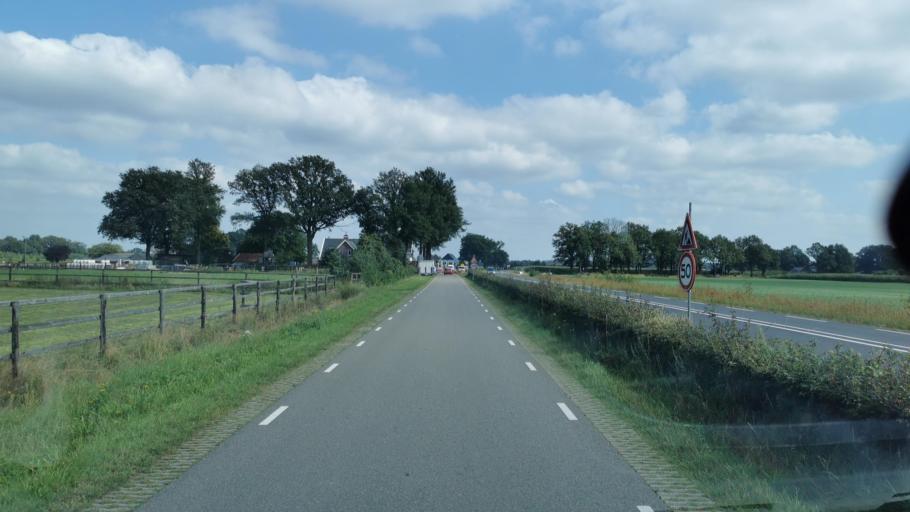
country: NL
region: Overijssel
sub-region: Gemeente Oldenzaal
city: Oldenzaal
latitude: 52.3353
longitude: 6.8846
